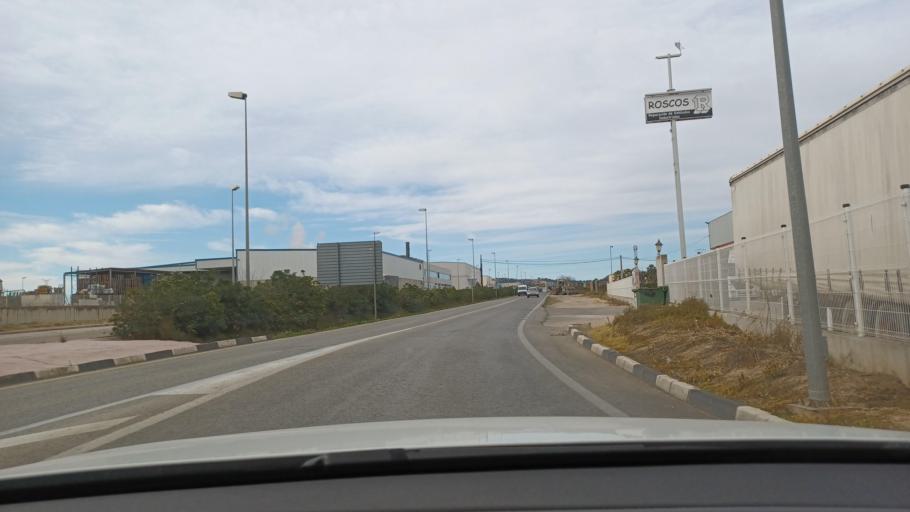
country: ES
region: Valencia
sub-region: Provincia de Valencia
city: Benifaio
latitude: 39.2885
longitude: -0.4426
